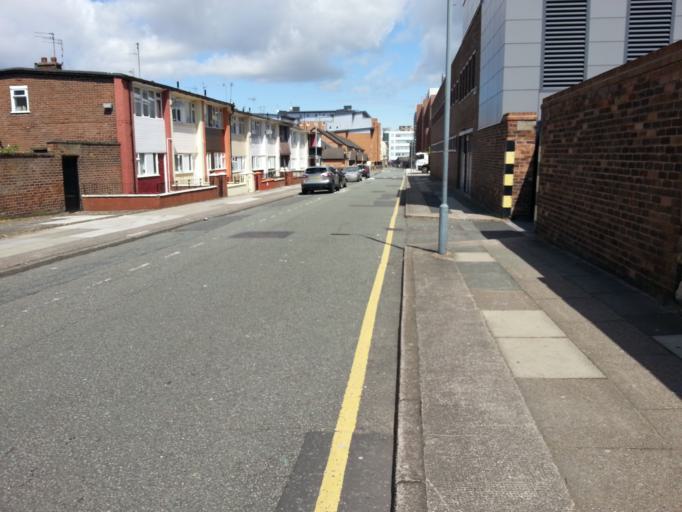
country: GB
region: England
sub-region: Liverpool
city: Liverpool
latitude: 53.4065
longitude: -2.9699
